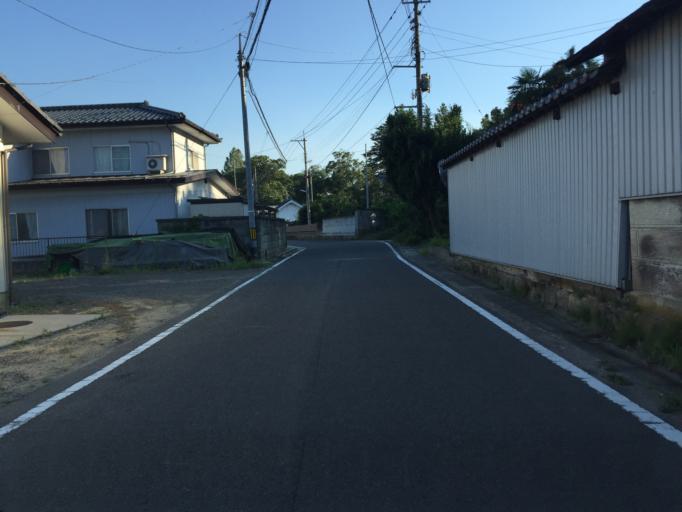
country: JP
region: Fukushima
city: Hobaramachi
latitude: 37.8772
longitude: 140.5190
